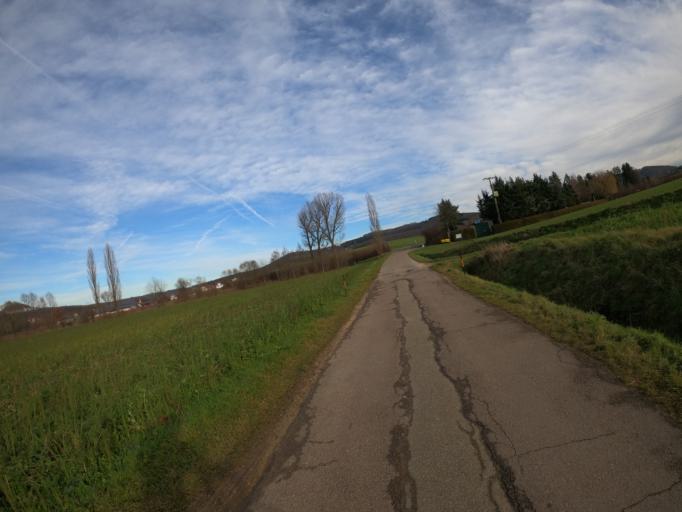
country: DE
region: Baden-Wuerttemberg
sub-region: Regierungsbezirk Stuttgart
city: Salach
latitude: 48.7021
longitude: 9.7317
